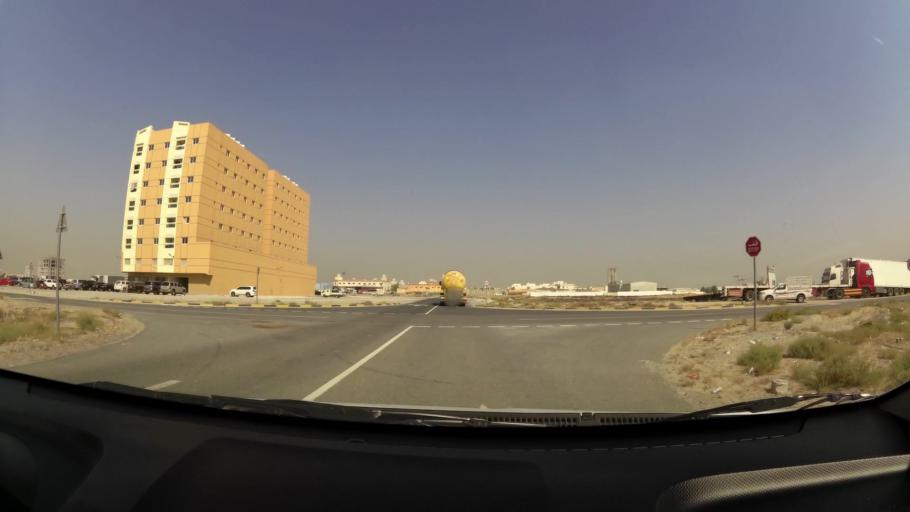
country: AE
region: Ajman
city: Ajman
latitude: 25.4253
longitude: 55.5356
